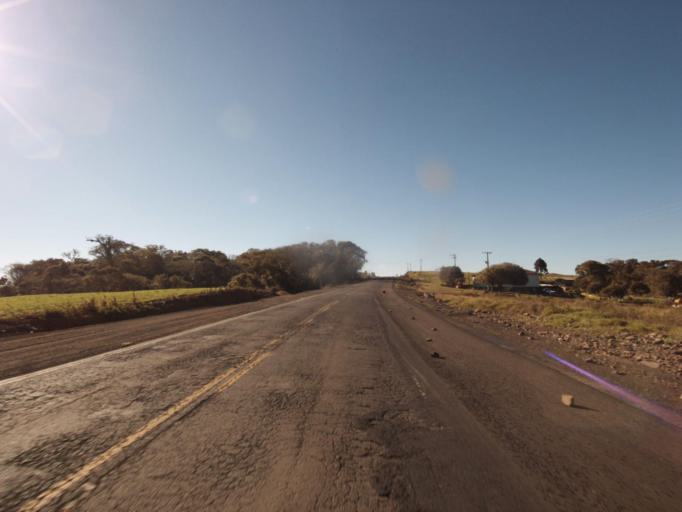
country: AR
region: Misiones
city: Bernardo de Irigoyen
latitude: -26.6458
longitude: -53.5192
